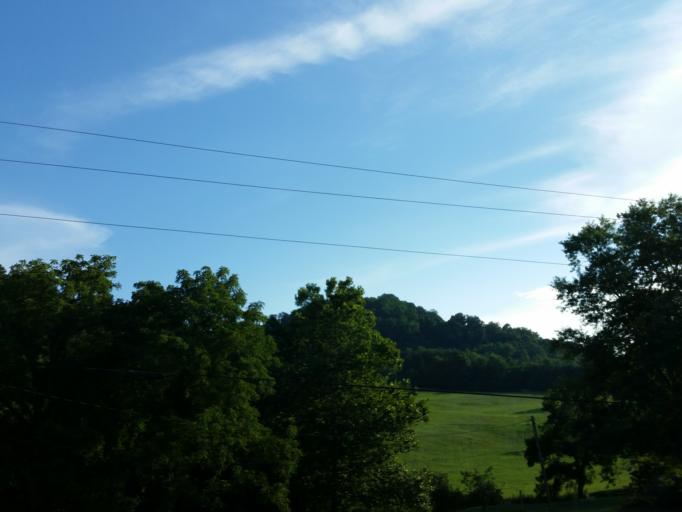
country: US
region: Tennessee
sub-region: Blount County
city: Eagleton Village
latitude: 35.8509
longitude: -83.9093
